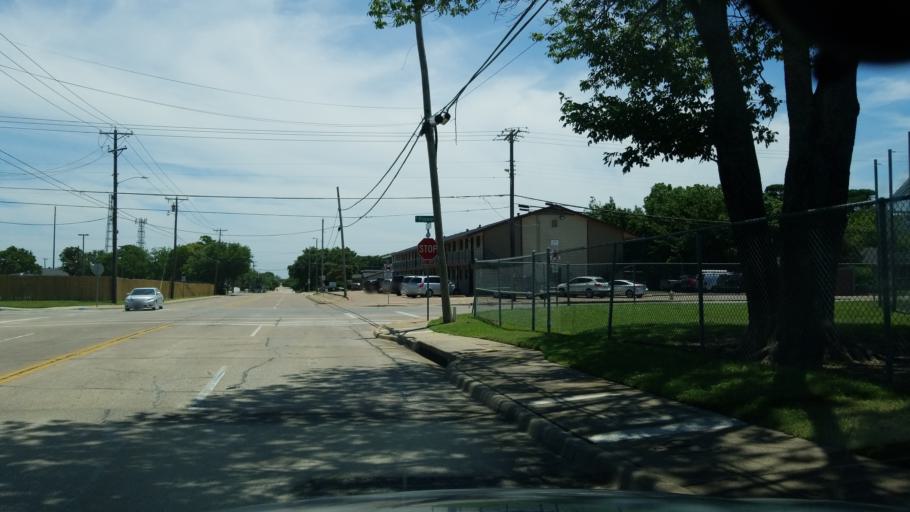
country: US
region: Texas
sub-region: Dallas County
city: Irving
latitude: 32.8179
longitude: -96.9257
